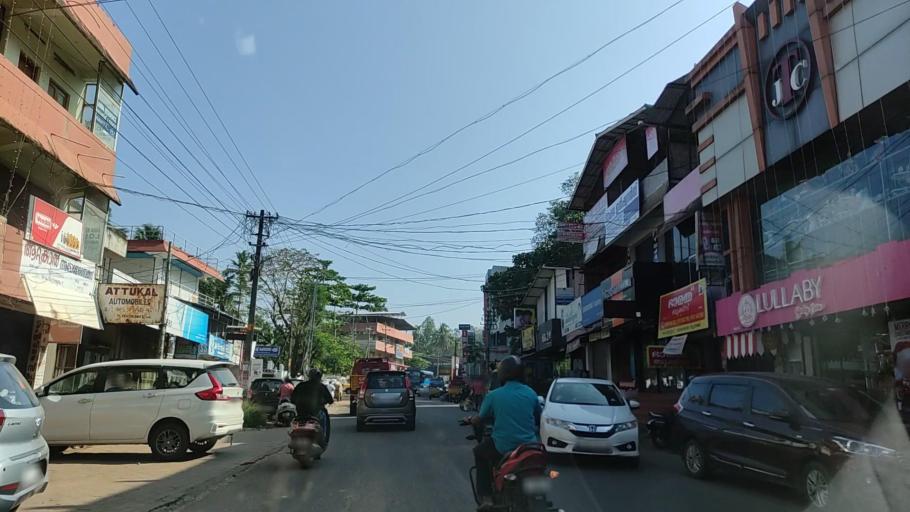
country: IN
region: Kerala
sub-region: Kollam
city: Punalur
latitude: 8.8984
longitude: 76.8614
